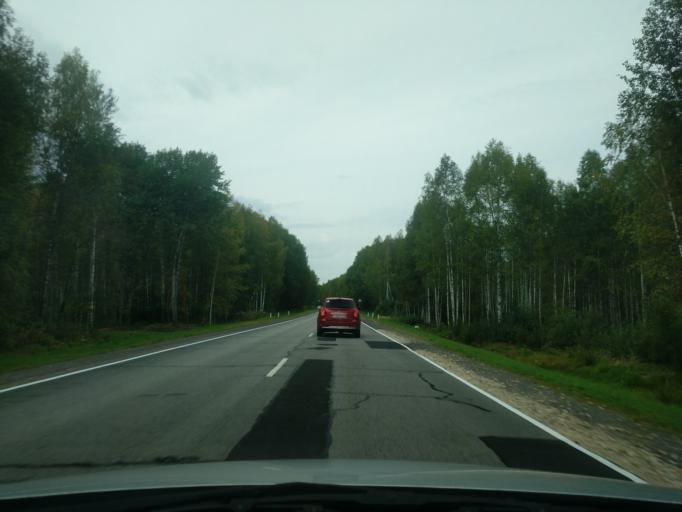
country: RU
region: Kirov
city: Kotel'nich
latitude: 58.2712
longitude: 48.0804
